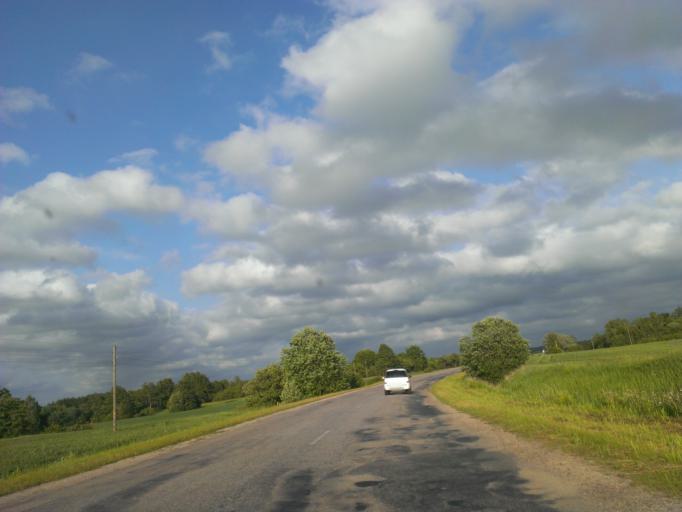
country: LV
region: Aizpute
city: Aizpute
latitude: 56.7346
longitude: 21.6904
